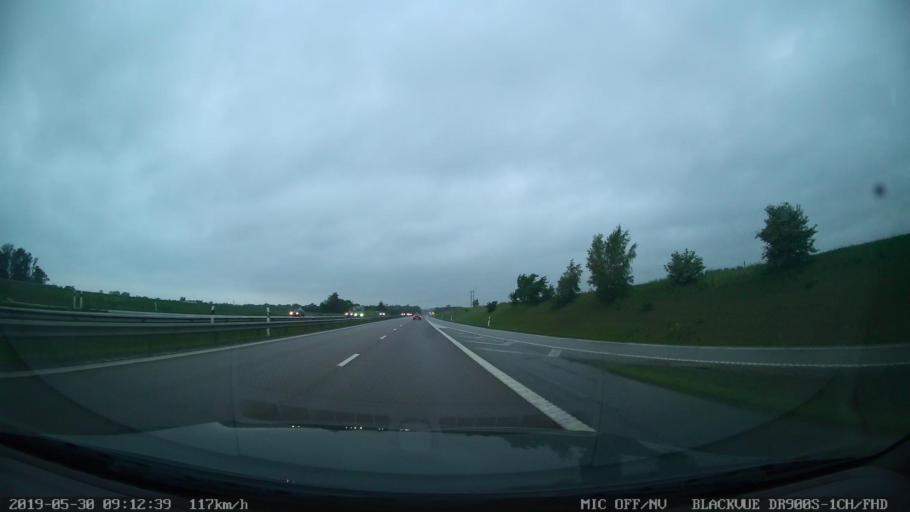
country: SE
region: Skane
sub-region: Helsingborg
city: Gantofta
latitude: 55.9684
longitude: 12.7951
